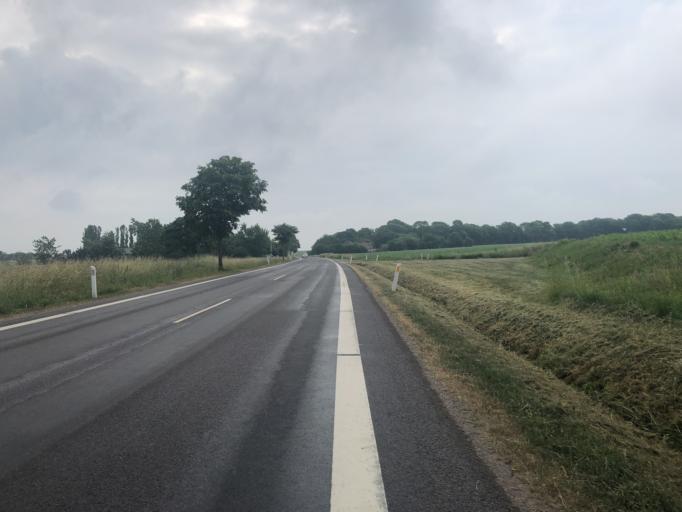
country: DK
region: Capital Region
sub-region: Bornholm Kommune
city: Akirkeby
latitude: 55.1531
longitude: 14.9150
